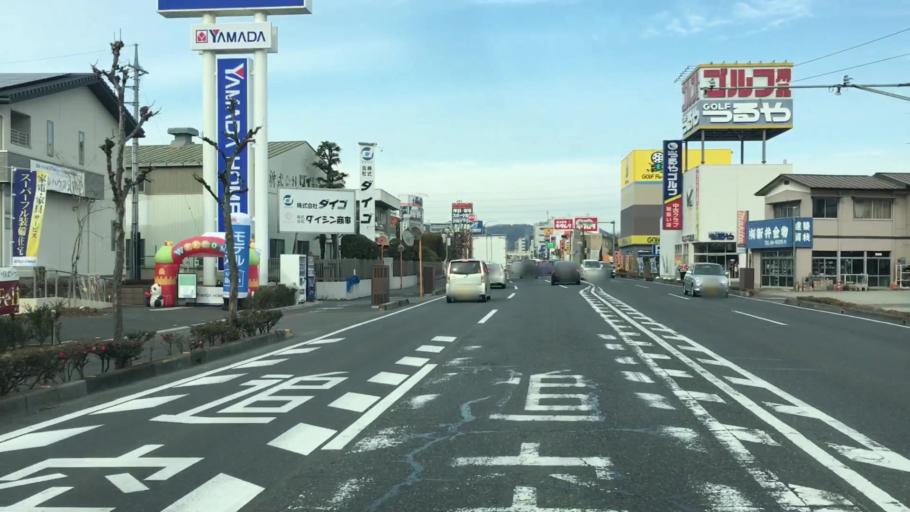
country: JP
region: Gunma
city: Ota
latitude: 36.2794
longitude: 139.3772
